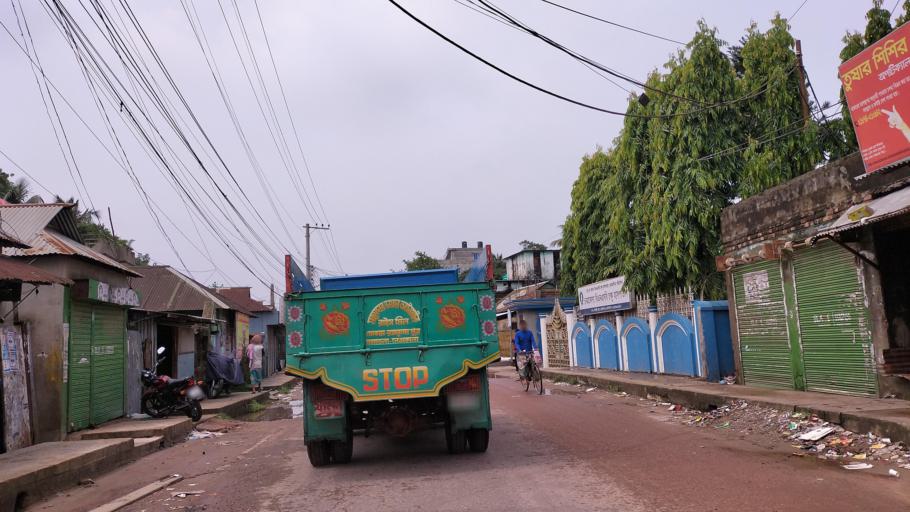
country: BD
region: Dhaka
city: Netrakona
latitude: 24.8882
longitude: 90.7381
